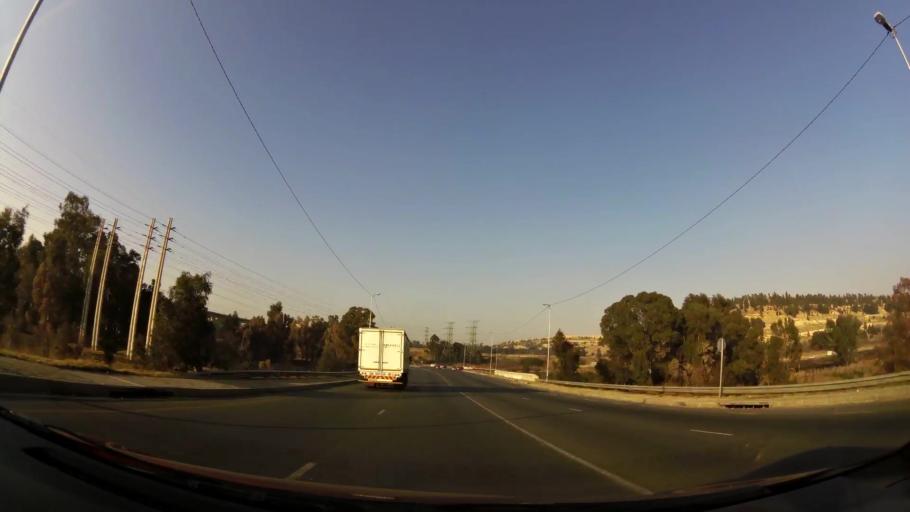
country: ZA
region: Gauteng
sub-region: City of Johannesburg Metropolitan Municipality
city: Johannesburg
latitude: -26.2204
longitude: 27.9810
